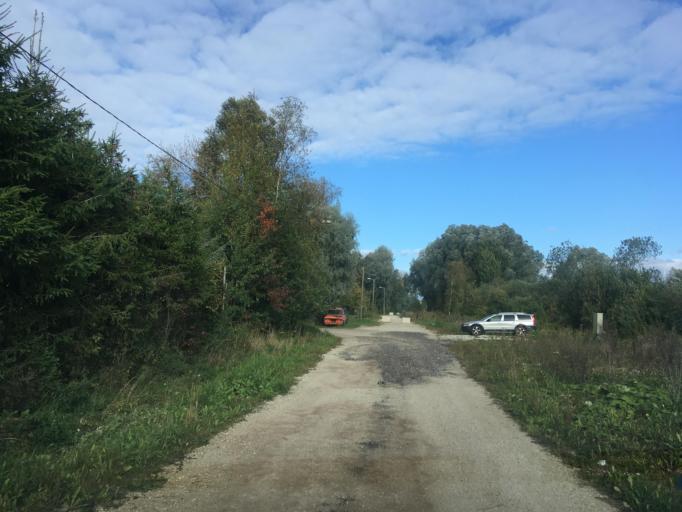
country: EE
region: Harju
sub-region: Joelaehtme vald
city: Loo
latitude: 59.4433
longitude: 24.9815
